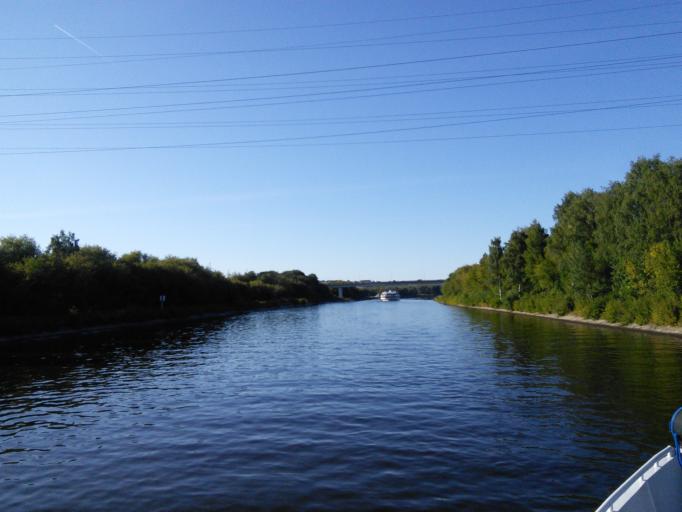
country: RU
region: Moskovskaya
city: Yakhroma
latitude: 56.2895
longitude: 37.4959
